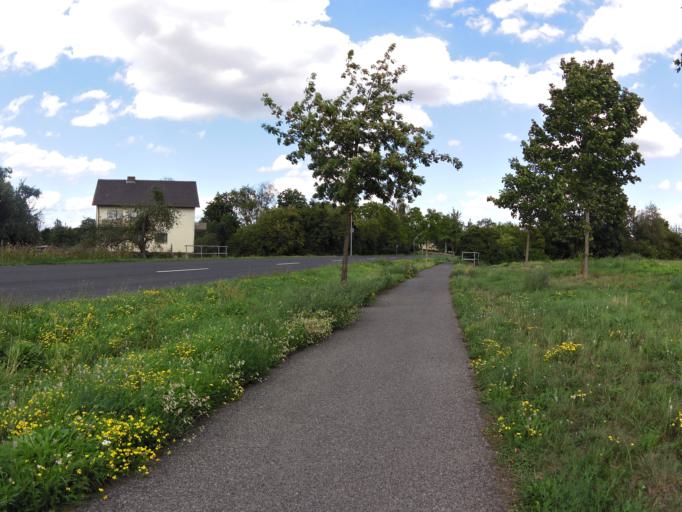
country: DE
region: Bavaria
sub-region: Regierungsbezirk Unterfranken
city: Bergrheinfeld
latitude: 49.9999
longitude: 10.1742
